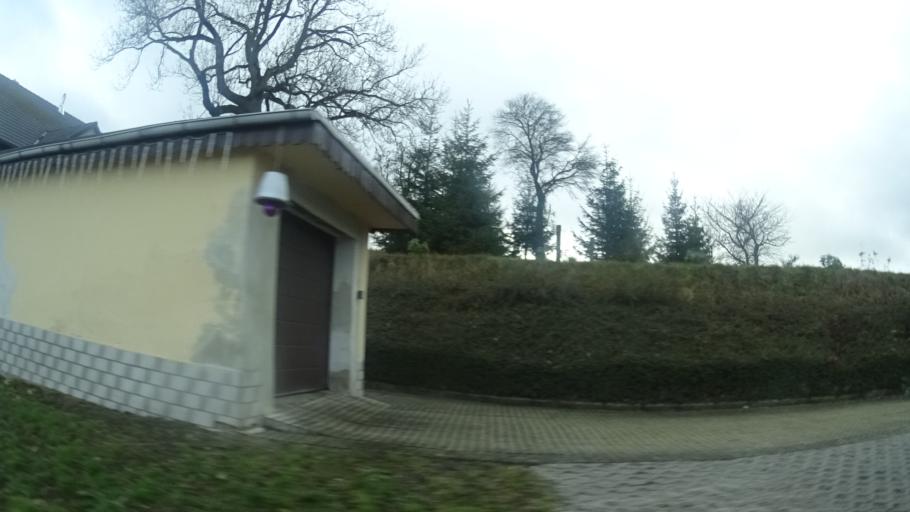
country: DE
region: Thuringia
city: Wittgendorf
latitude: 50.6027
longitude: 11.2462
